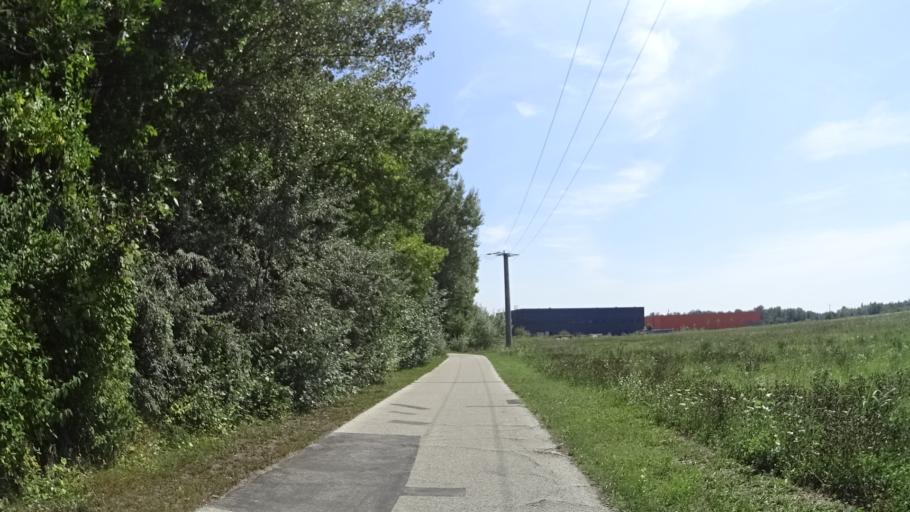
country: HU
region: Fejer
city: Pakozd
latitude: 47.2250
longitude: 18.5646
